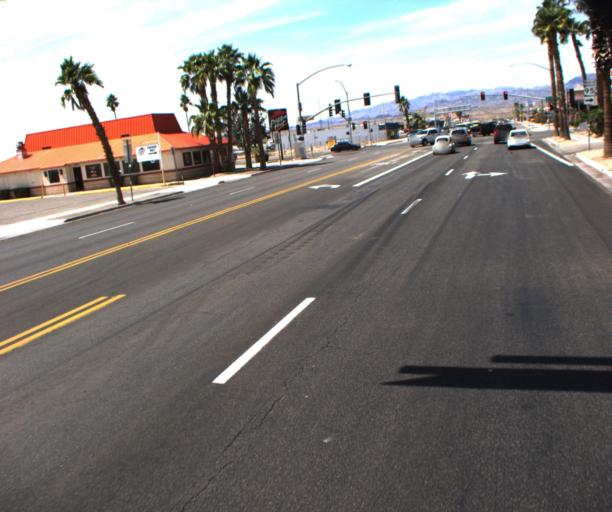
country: US
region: Arizona
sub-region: La Paz County
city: Parker
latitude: 34.1497
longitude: -114.2886
